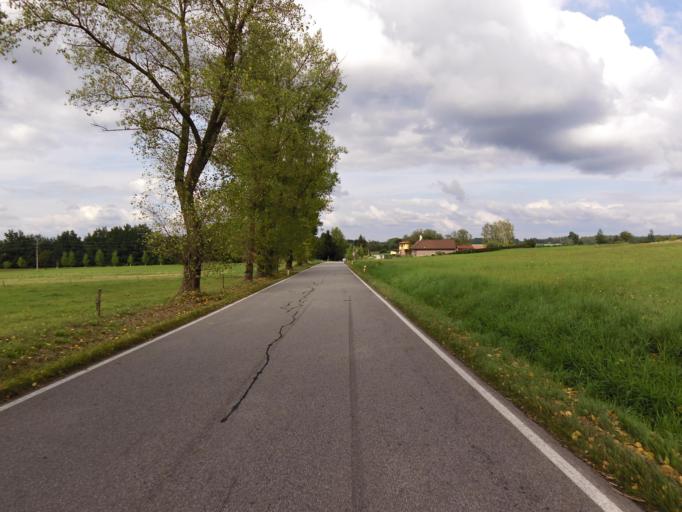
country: CZ
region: Jihocesky
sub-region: Okres Ceske Budejovice
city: Nove Hrady
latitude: 48.7989
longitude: 14.7908
